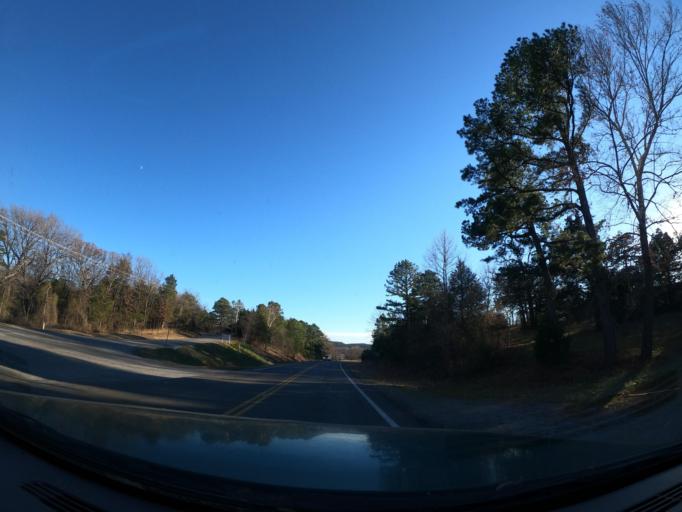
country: US
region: Oklahoma
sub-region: Latimer County
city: Wilburton
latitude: 34.9519
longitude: -95.3421
